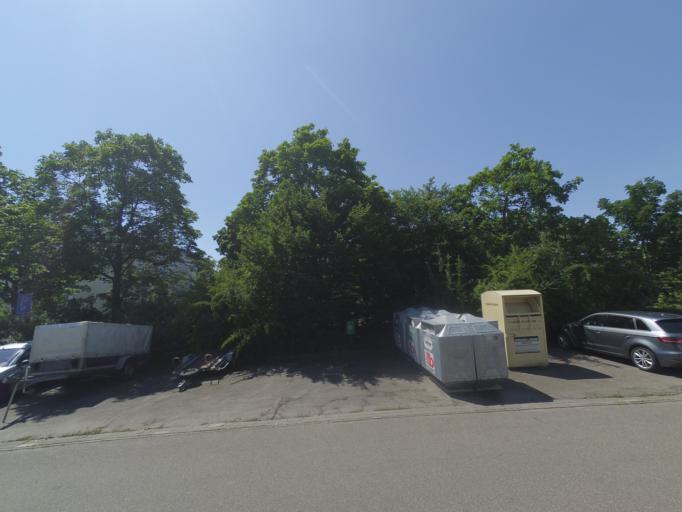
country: DE
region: Hesse
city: Viernheim
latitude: 49.5494
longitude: 8.5764
